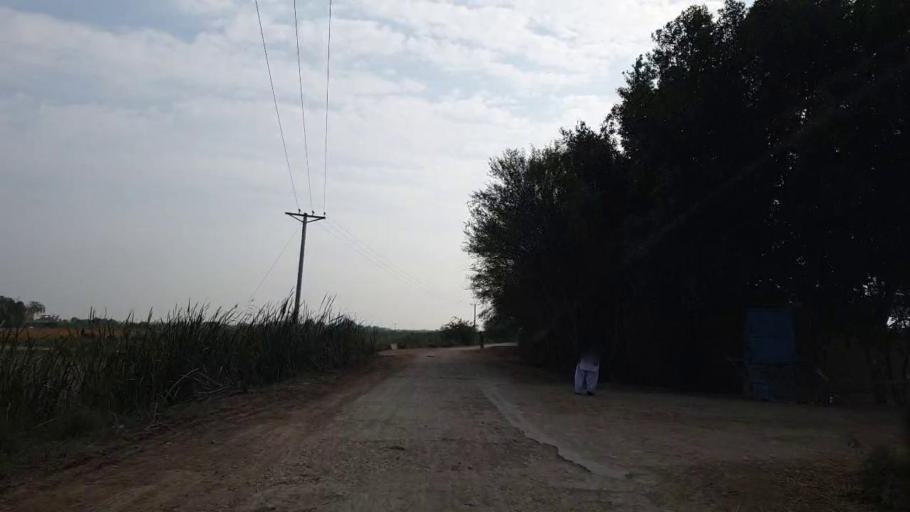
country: PK
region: Sindh
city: Tando Muhammad Khan
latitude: 25.0263
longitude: 68.4467
